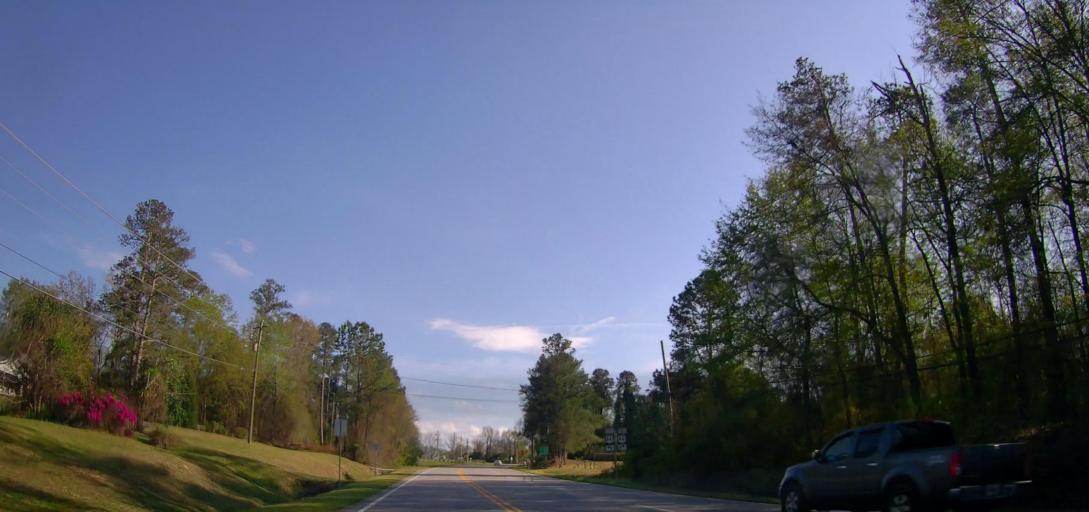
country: US
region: Georgia
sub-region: Baldwin County
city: Hardwick
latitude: 33.0261
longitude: -83.2349
